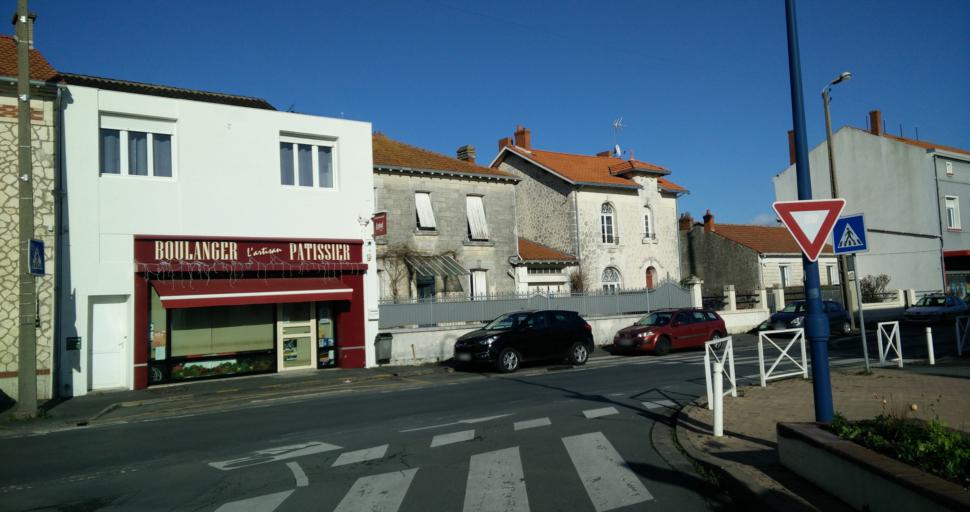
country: FR
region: Poitou-Charentes
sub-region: Departement de la Charente-Maritime
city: La Rochelle
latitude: 46.1641
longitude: -1.2038
